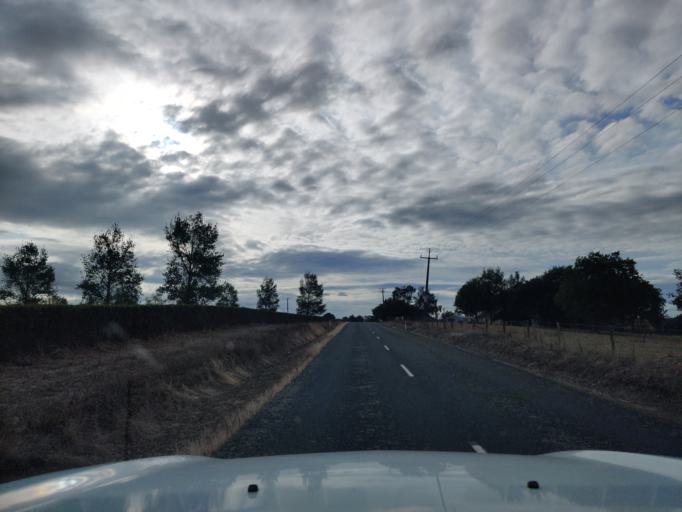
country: NZ
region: Waikato
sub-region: Waipa District
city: Cambridge
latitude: -37.7953
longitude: 175.4368
